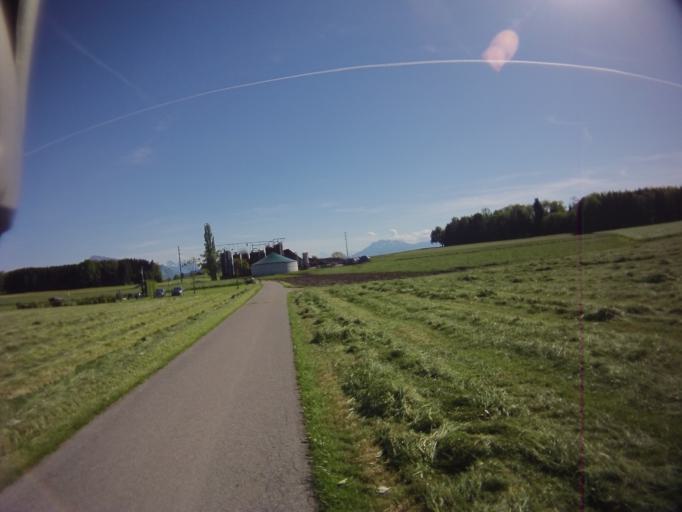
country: CH
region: Zurich
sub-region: Bezirk Affoltern
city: Knonau
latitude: 47.2060
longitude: 8.4485
